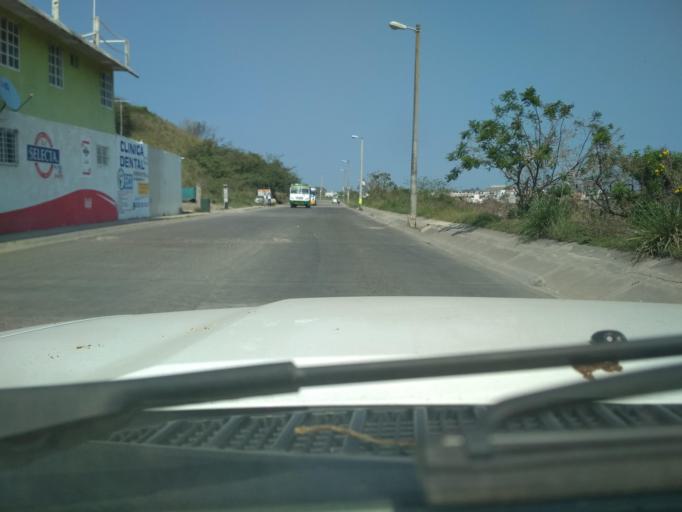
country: MX
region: Veracruz
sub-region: Veracruz
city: Lomas de Rio Medio Cuatro
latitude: 19.1960
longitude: -96.2081
